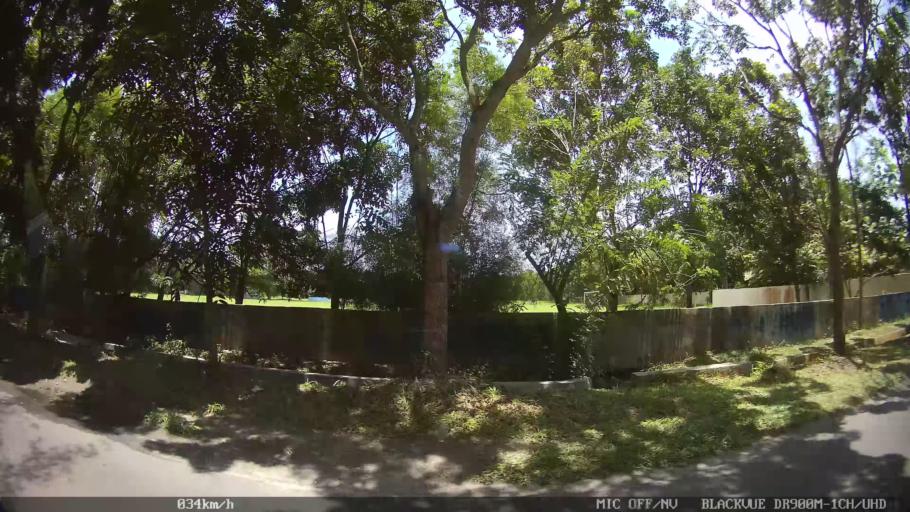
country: ID
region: North Sumatra
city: Percut
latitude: 3.5415
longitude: 98.8715
